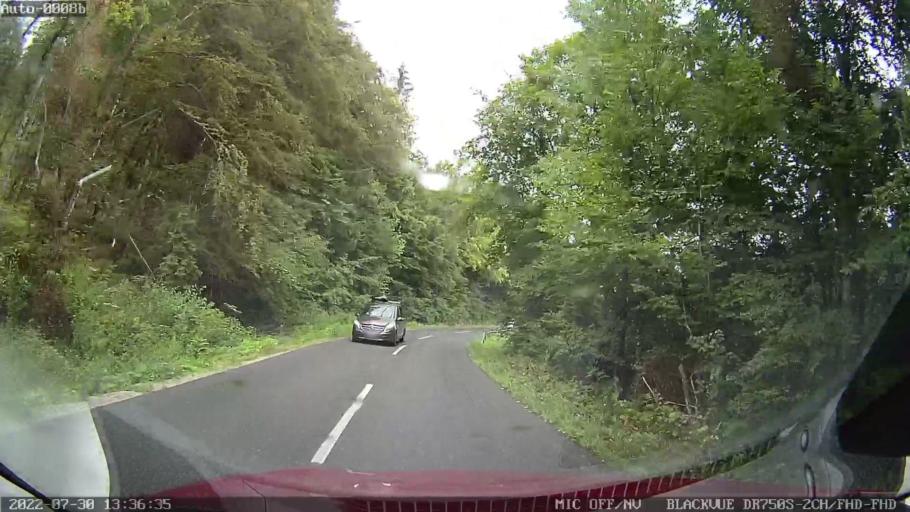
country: SI
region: Zuzemberk
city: Zuzemberk
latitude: 45.8712
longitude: 14.9235
